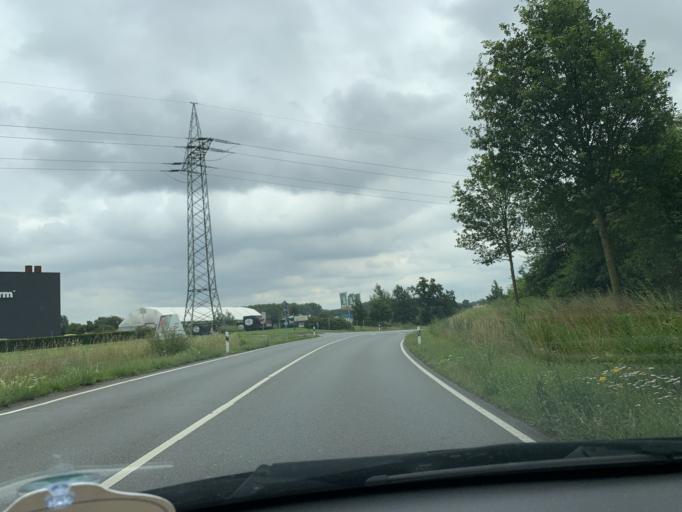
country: DE
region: North Rhine-Westphalia
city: Oelde
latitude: 51.8116
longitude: 8.1274
